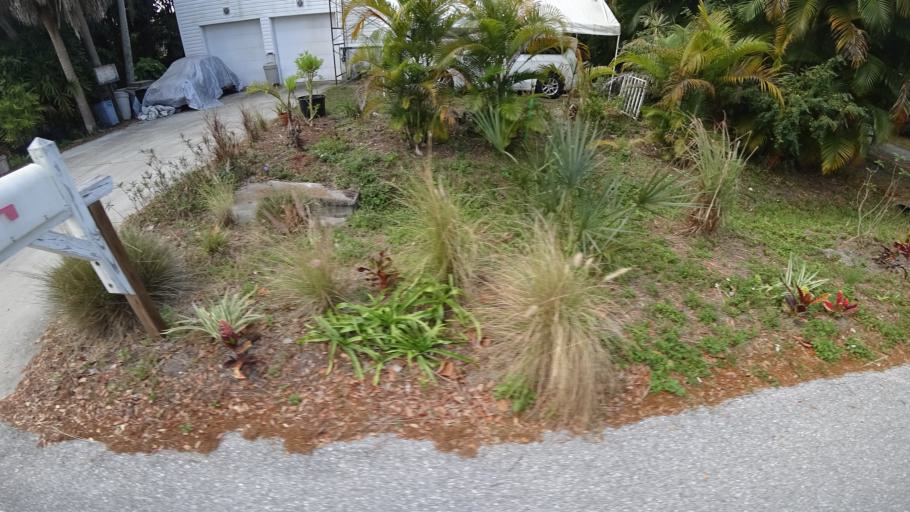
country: US
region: Florida
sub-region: Manatee County
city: Whitfield
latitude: 27.4205
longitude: -82.5528
